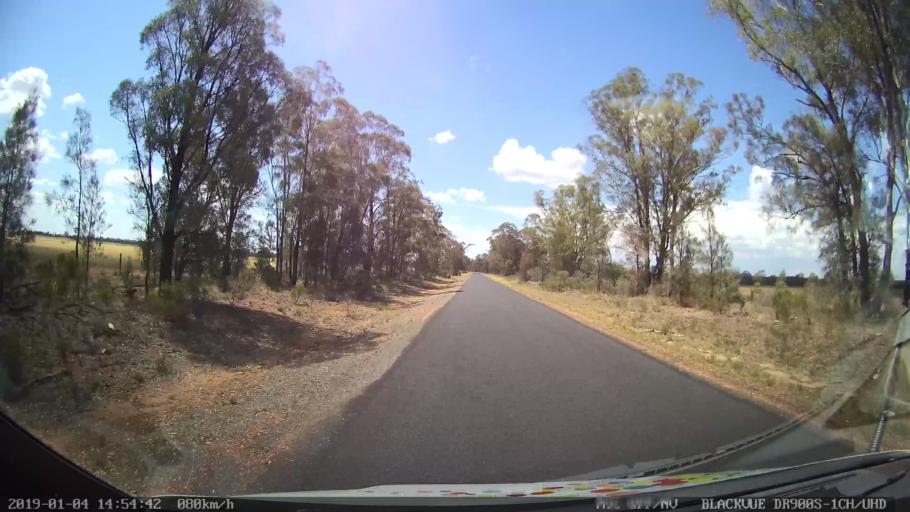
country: AU
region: New South Wales
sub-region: Dubbo Municipality
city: Dubbo
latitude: -31.9877
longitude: 148.6545
